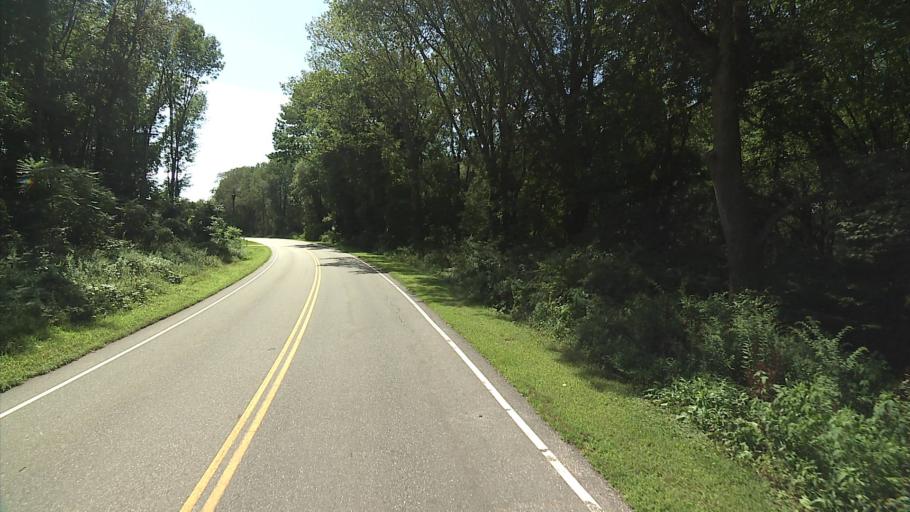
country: US
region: Connecticut
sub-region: Windham County
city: South Woodstock
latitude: 41.8250
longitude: -72.0343
